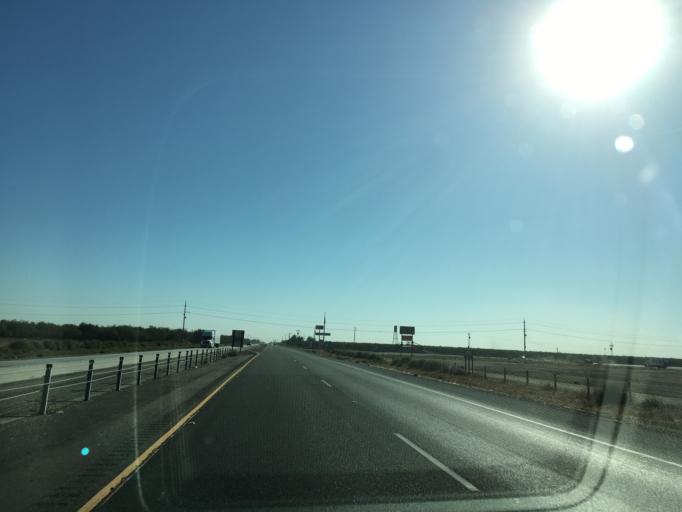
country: US
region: California
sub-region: Merced County
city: Dos Palos
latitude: 37.0835
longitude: -120.4767
